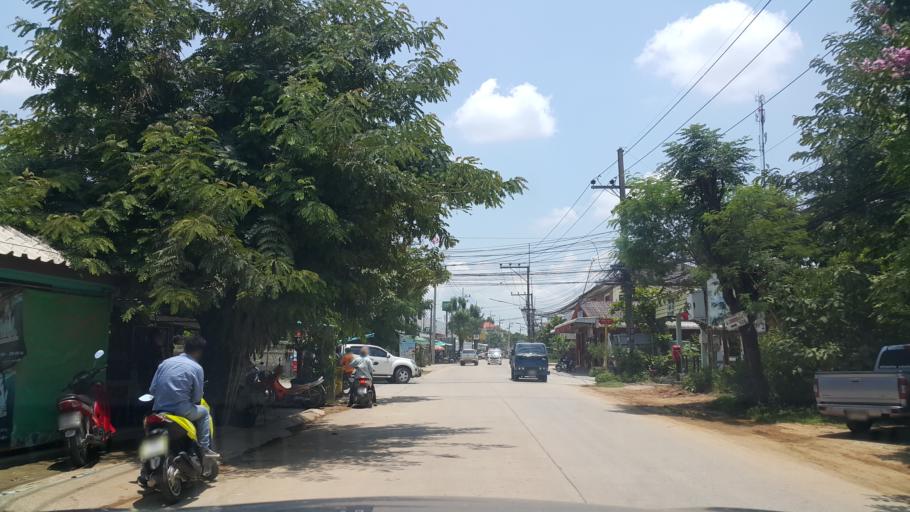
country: TH
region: Chiang Rai
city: Chiang Rai
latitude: 19.9297
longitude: 99.8156
